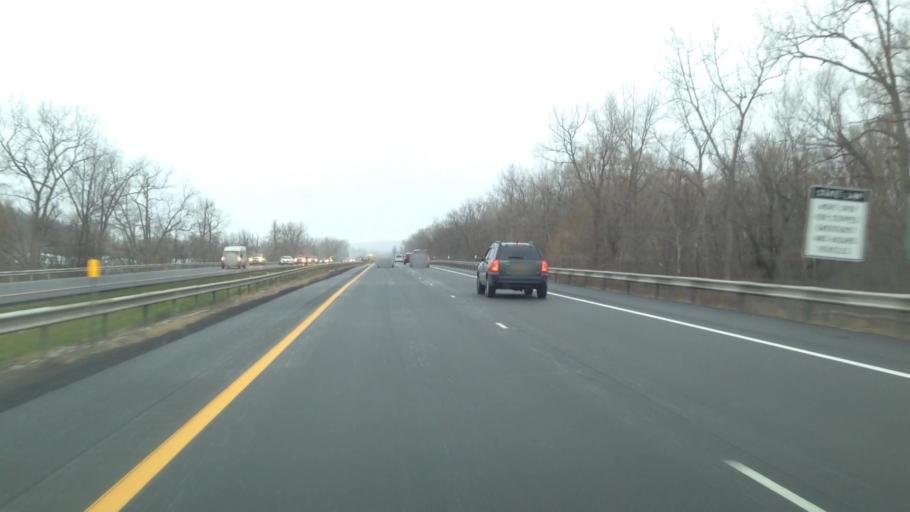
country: US
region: New York
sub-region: Montgomery County
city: Fort Plain
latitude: 42.9208
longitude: -74.6116
